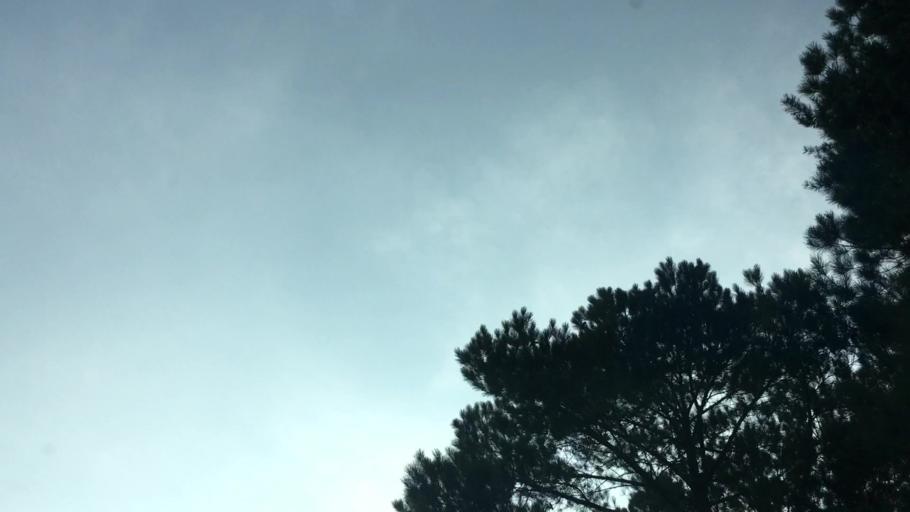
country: US
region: Alabama
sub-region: Bibb County
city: Woodstock
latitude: 33.2154
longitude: -87.0769
